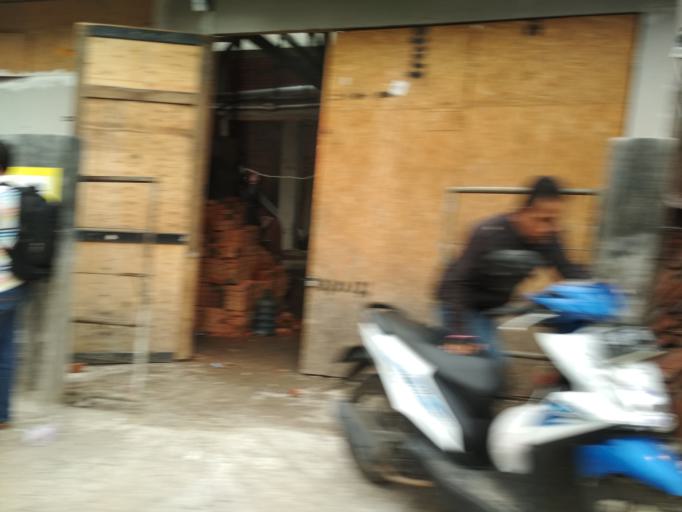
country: ID
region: West Java
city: Bogor
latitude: -6.5939
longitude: 106.7775
